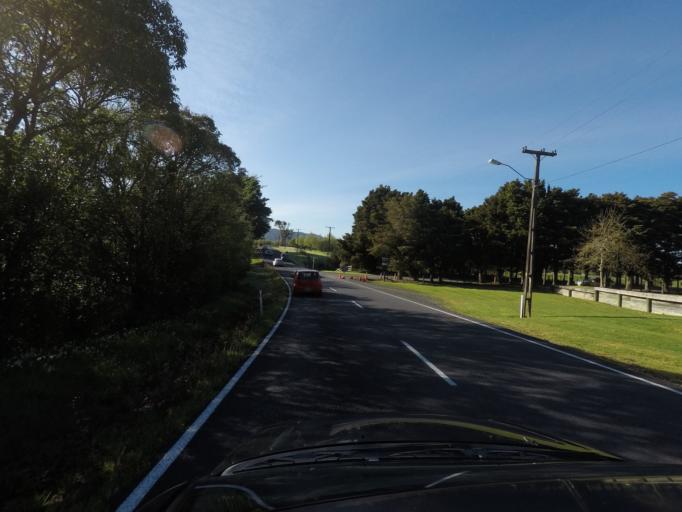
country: NZ
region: Auckland
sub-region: Auckland
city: Red Hill
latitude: -37.0015
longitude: 175.0408
